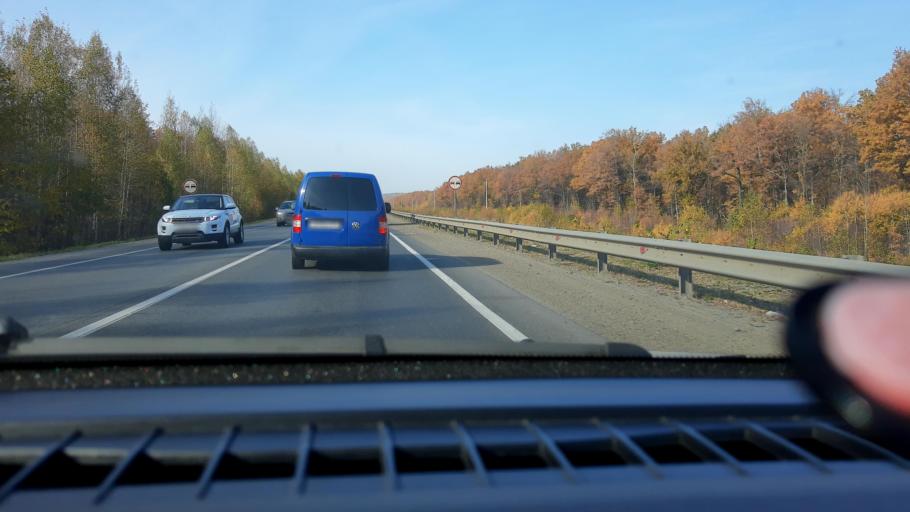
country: RU
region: Nizjnij Novgorod
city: Pamyat' Parizhskoy Kommuny
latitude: 56.0815
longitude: 44.3582
